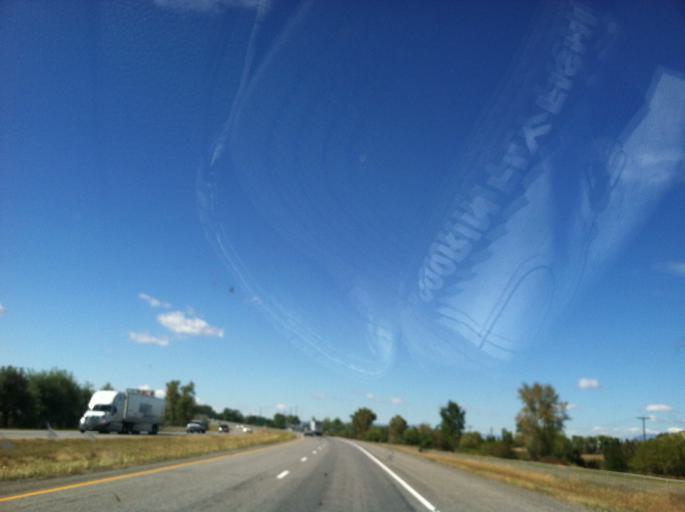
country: US
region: Montana
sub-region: Gallatin County
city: Bozeman
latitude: 45.6870
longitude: -111.0170
